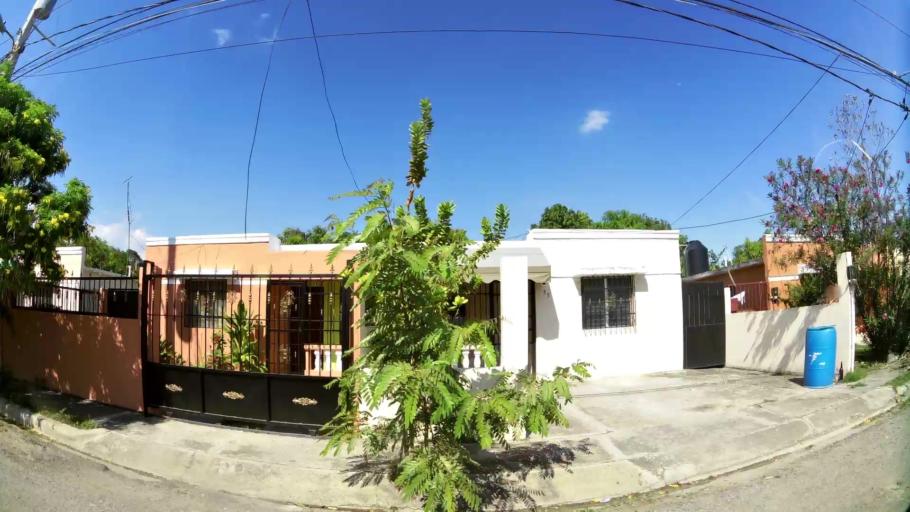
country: DO
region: Santo Domingo
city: Santo Domingo Oeste
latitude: 18.4726
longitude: -70.0095
